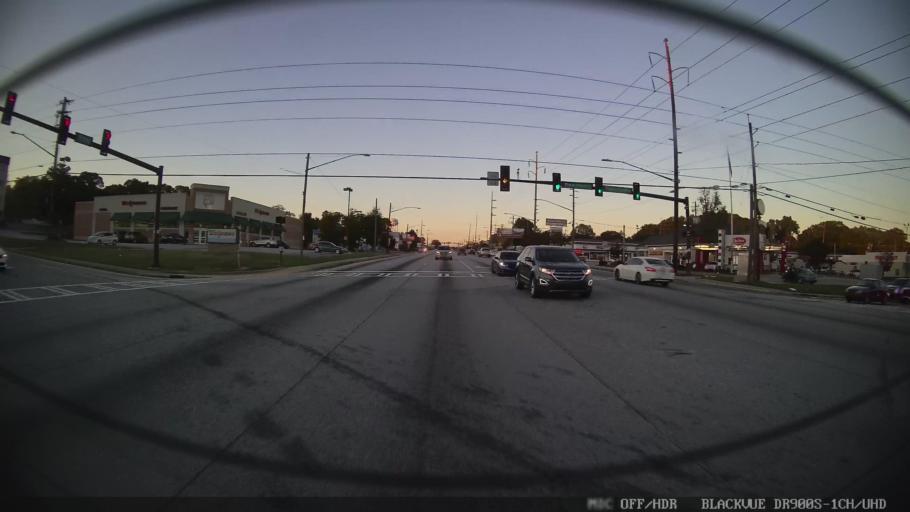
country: US
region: Georgia
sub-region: Clayton County
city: Riverdale
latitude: 33.5728
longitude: -84.4126
